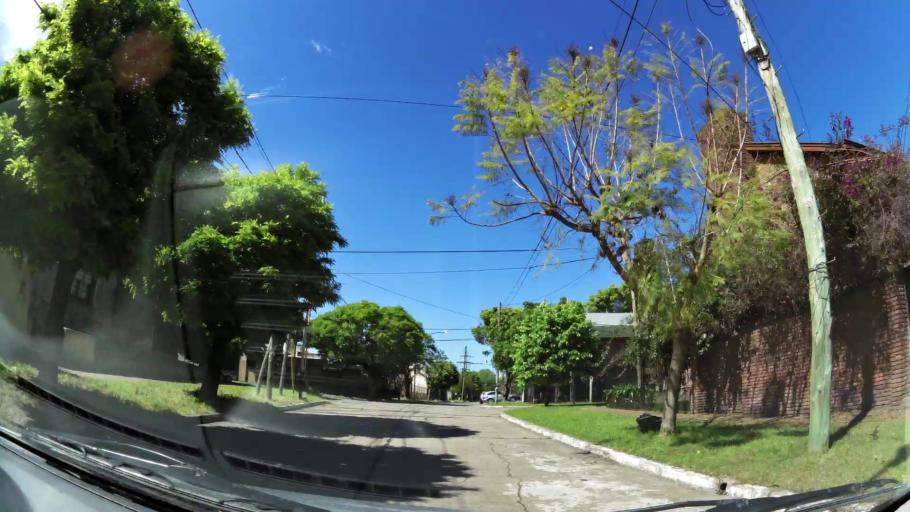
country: AR
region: Buenos Aires
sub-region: Partido de Quilmes
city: Quilmes
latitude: -34.6995
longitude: -58.3028
